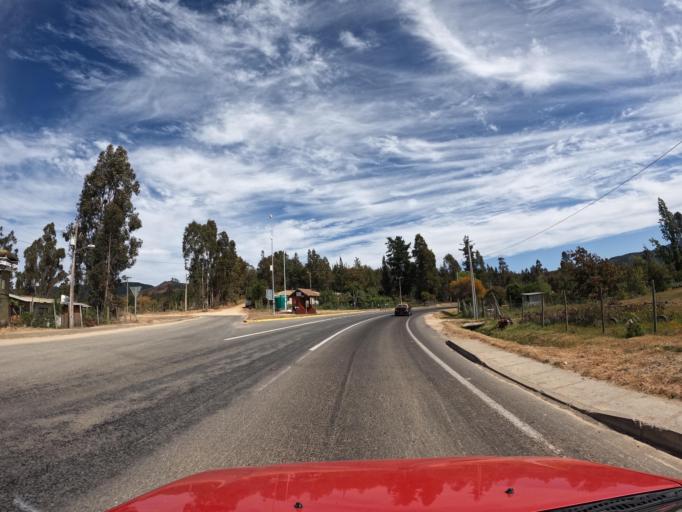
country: CL
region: Maule
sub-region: Provincia de Talca
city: Talca
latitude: -35.1286
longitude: -71.9554
